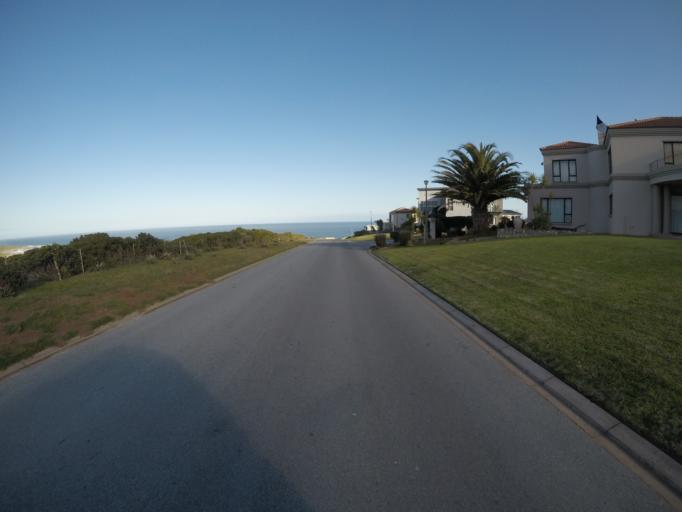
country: ZA
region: Western Cape
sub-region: Eden District Municipality
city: Riversdale
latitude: -34.4172
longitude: 21.3466
